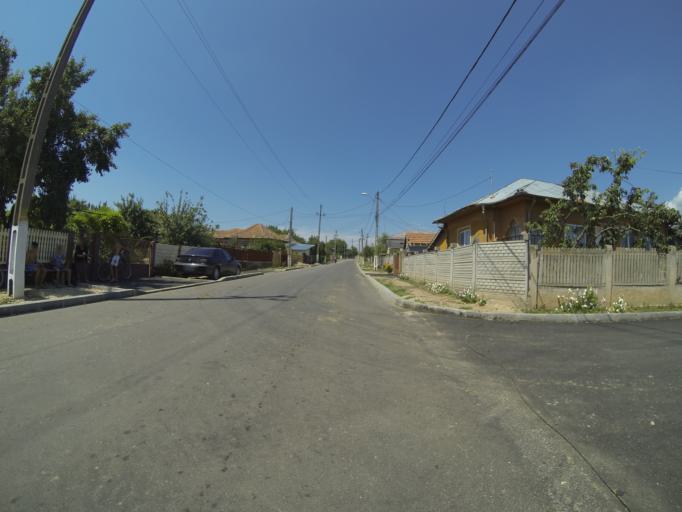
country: RO
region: Dolj
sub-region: Comuna Segarcea
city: Segarcea
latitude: 44.0972
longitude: 23.7344
